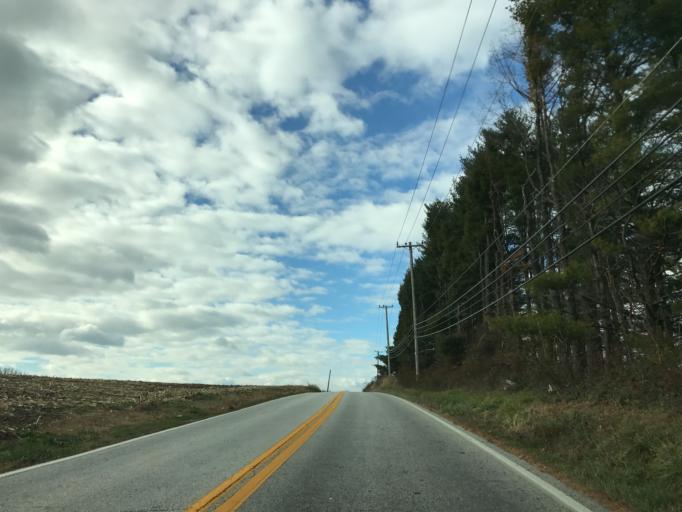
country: US
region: Maryland
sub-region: Harford County
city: Jarrettsville
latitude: 39.5120
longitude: -76.5159
